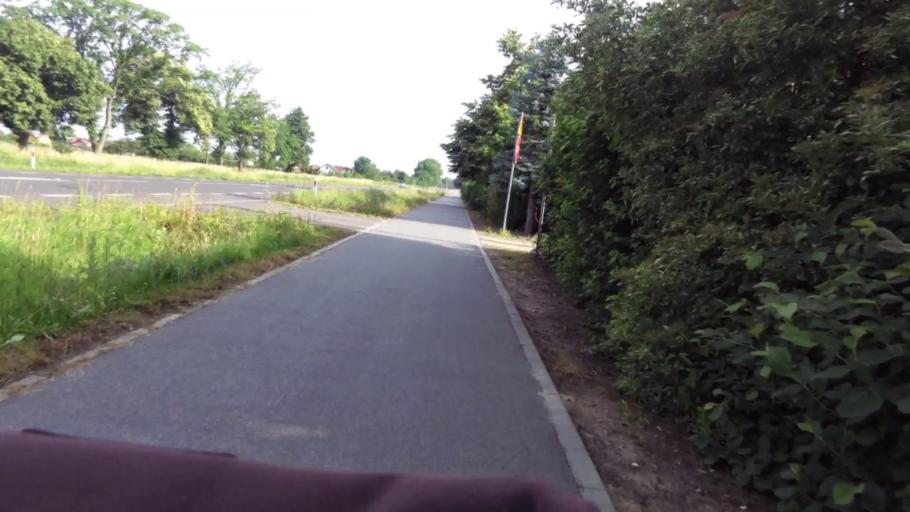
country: PL
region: West Pomeranian Voivodeship
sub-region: Powiat kamienski
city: Dziwnow
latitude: 54.0192
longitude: 14.8108
